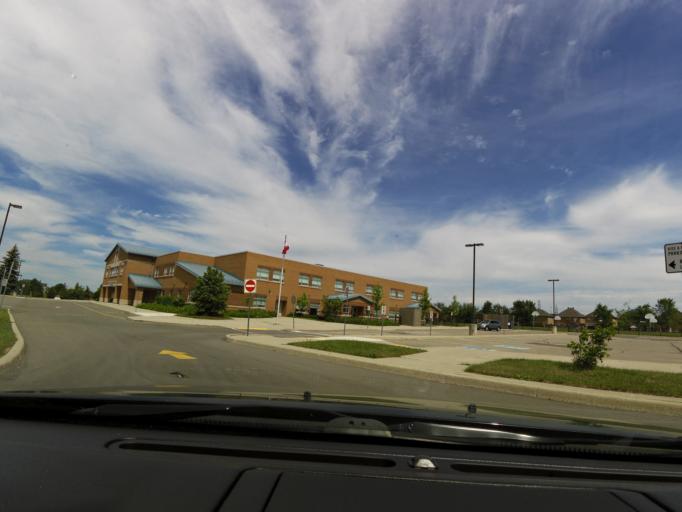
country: CA
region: Ontario
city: Mississauga
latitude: 43.5407
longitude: -79.7236
